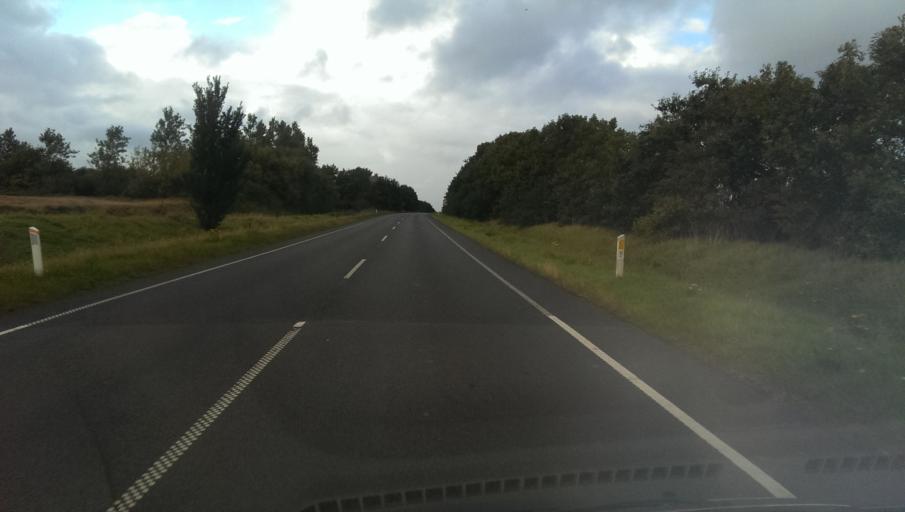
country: DK
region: South Denmark
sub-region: Varde Kommune
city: Olgod
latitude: 55.7602
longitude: 8.6201
